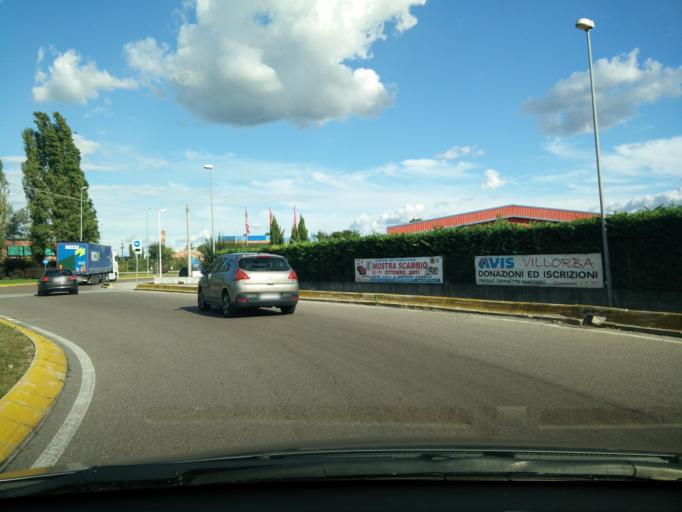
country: IT
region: Veneto
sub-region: Provincia di Treviso
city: Lancenigo-Villorba
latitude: 45.7351
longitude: 12.2583
